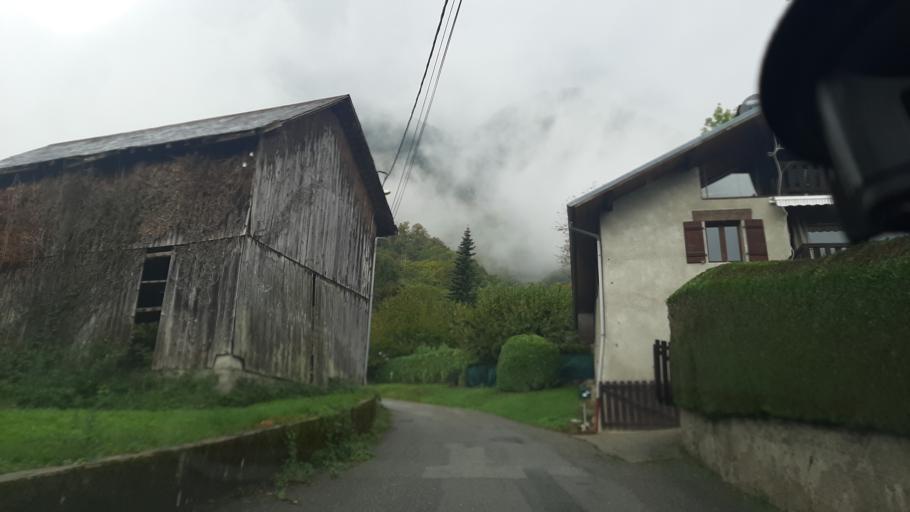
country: FR
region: Rhone-Alpes
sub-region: Departement de la Savoie
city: Gresy-sur-Isere
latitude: 45.6214
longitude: 6.2833
